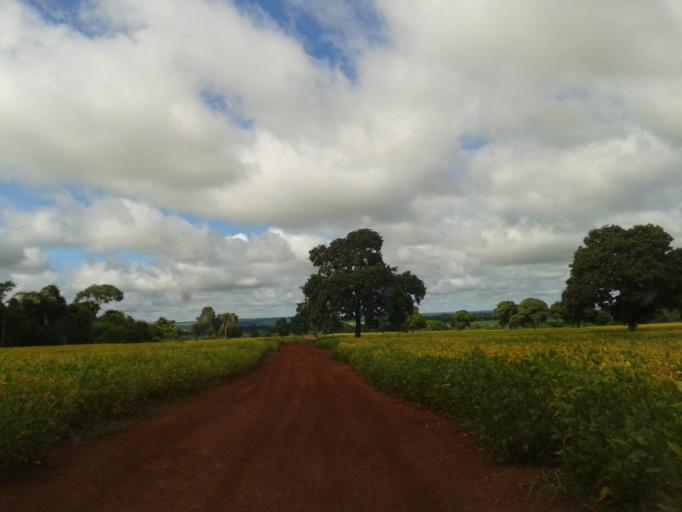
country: BR
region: Minas Gerais
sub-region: Santa Vitoria
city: Santa Vitoria
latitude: -18.7610
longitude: -49.8489
